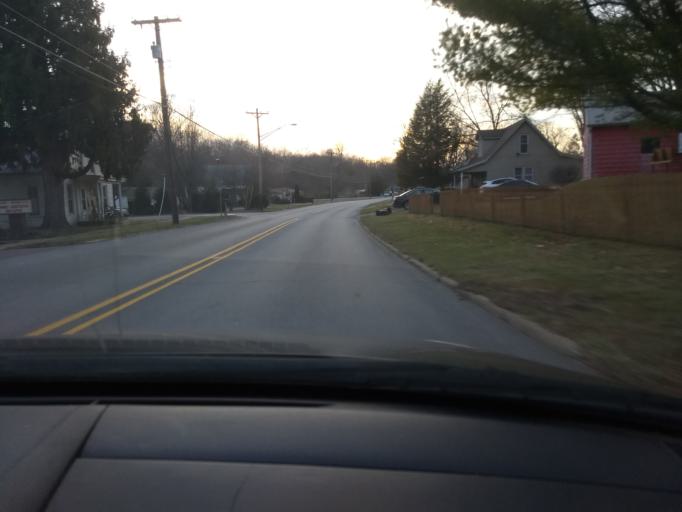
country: US
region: Indiana
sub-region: Floyd County
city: Georgetown
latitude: 38.2945
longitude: -85.9793
